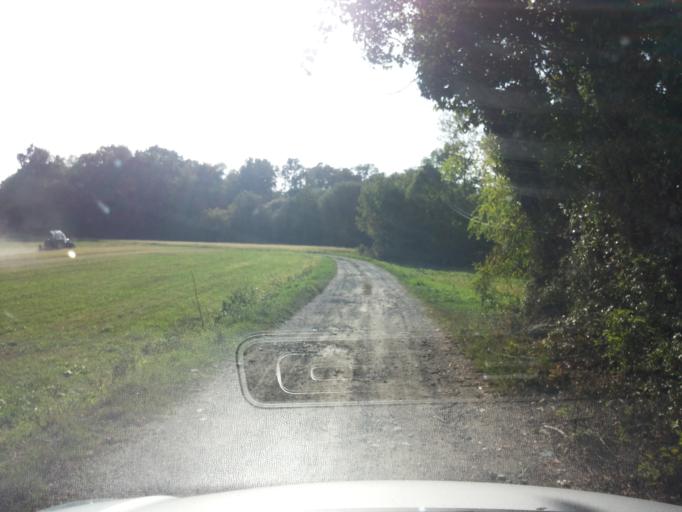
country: IT
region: Piedmont
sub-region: Provincia di Biella
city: Roppolo
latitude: 45.4371
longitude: 8.0769
